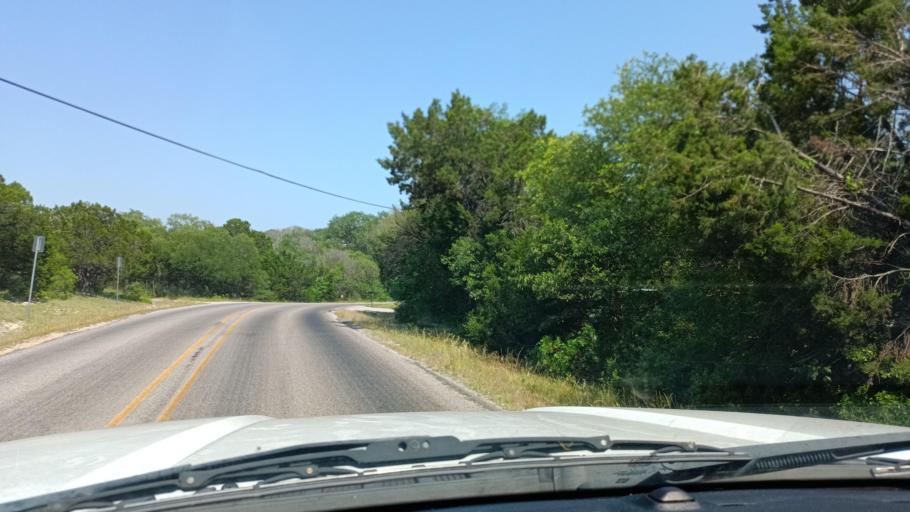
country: US
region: Texas
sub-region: Bell County
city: Morgans Point Resort
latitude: 31.1106
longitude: -97.5260
